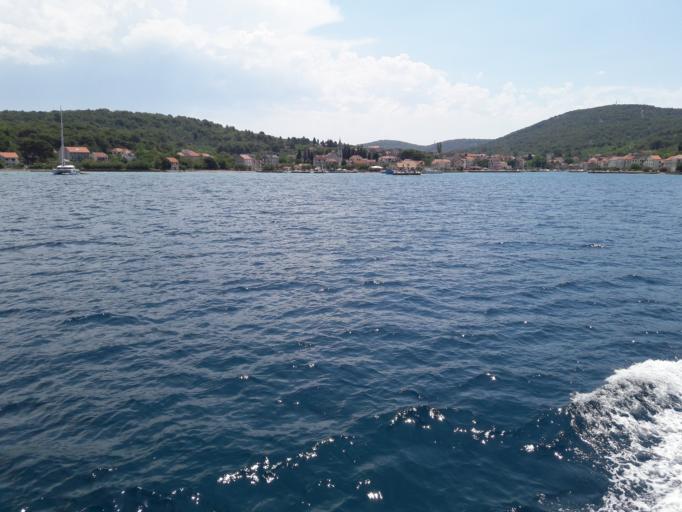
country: HR
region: Sibensko-Kniniska
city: Vodice
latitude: 43.7017
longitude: 15.8306
